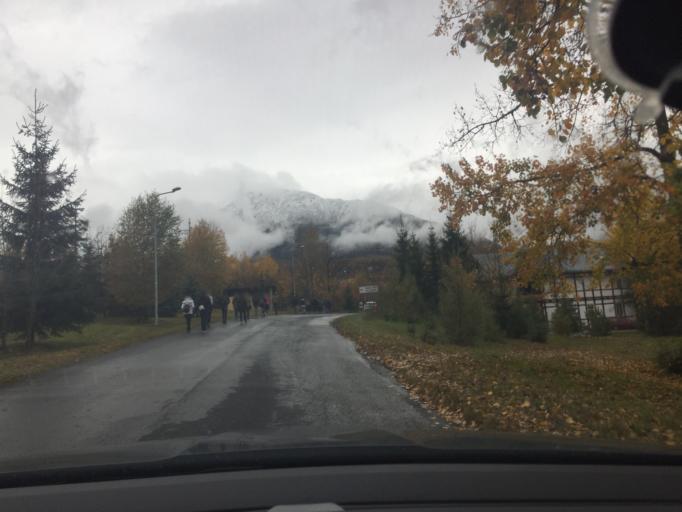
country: SK
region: Presovsky
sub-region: Okres Poprad
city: Vysoke Tatry
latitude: 49.1333
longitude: 20.2410
